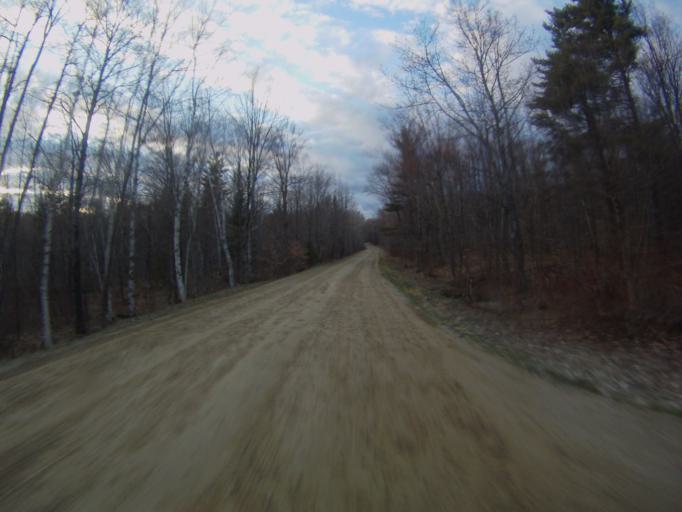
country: US
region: Vermont
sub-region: Rutland County
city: Brandon
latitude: 43.9055
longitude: -73.0165
